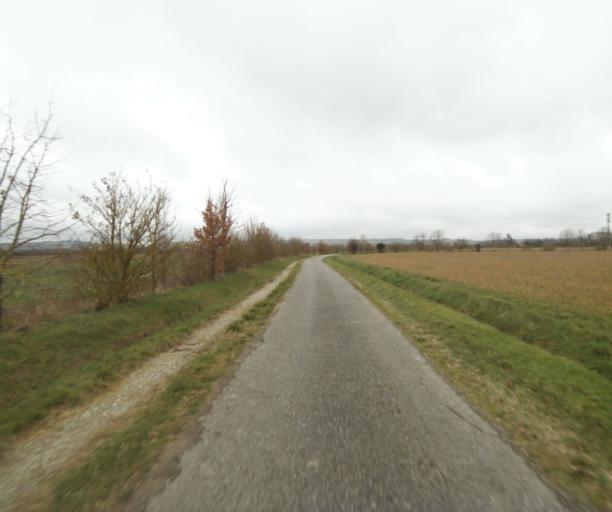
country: FR
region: Midi-Pyrenees
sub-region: Departement de l'Ariege
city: Mazeres
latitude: 43.2501
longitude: 1.6597
